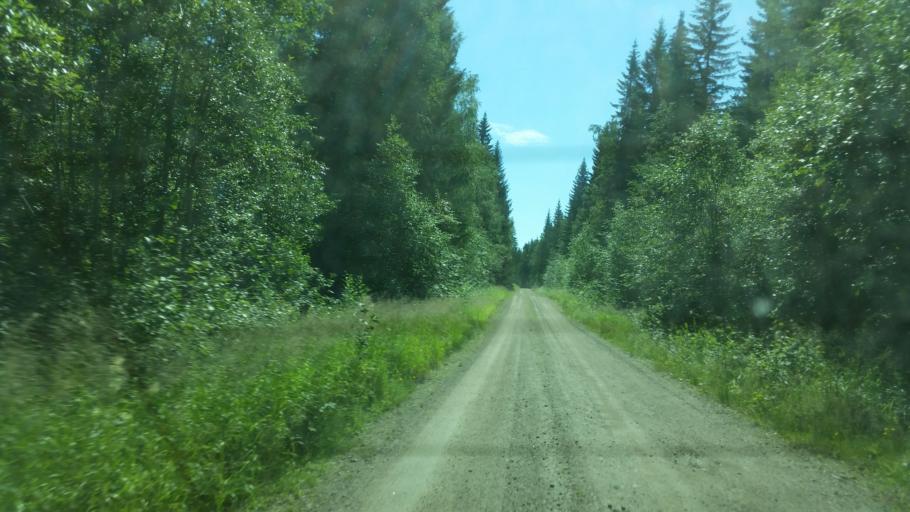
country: SE
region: Vaesternorrland
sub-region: Ange Kommun
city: Ange
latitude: 62.2341
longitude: 15.3915
